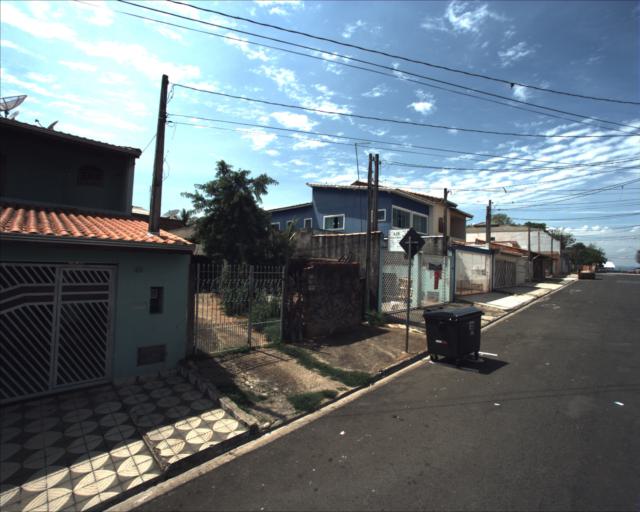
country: BR
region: Sao Paulo
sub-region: Sorocaba
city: Sorocaba
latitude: -23.4121
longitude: -47.4107
